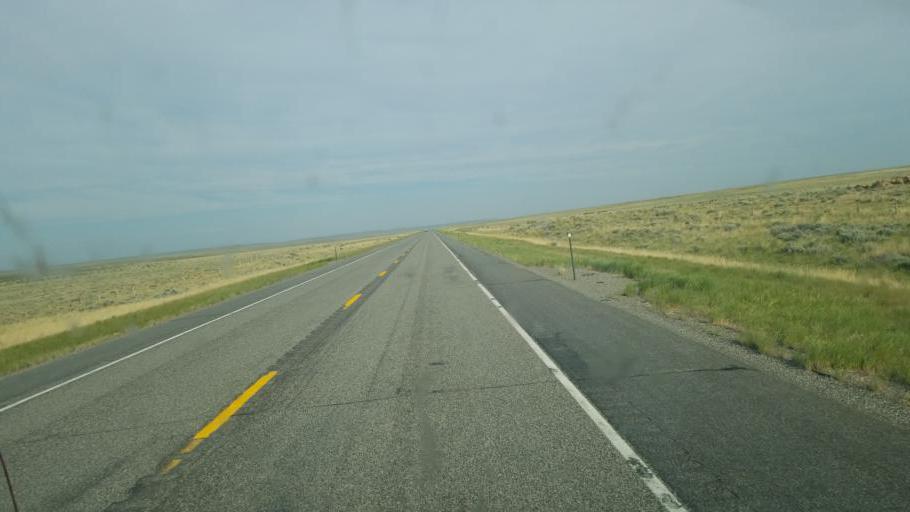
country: US
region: Wyoming
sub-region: Fremont County
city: Riverton
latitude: 43.1668
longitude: -107.7902
